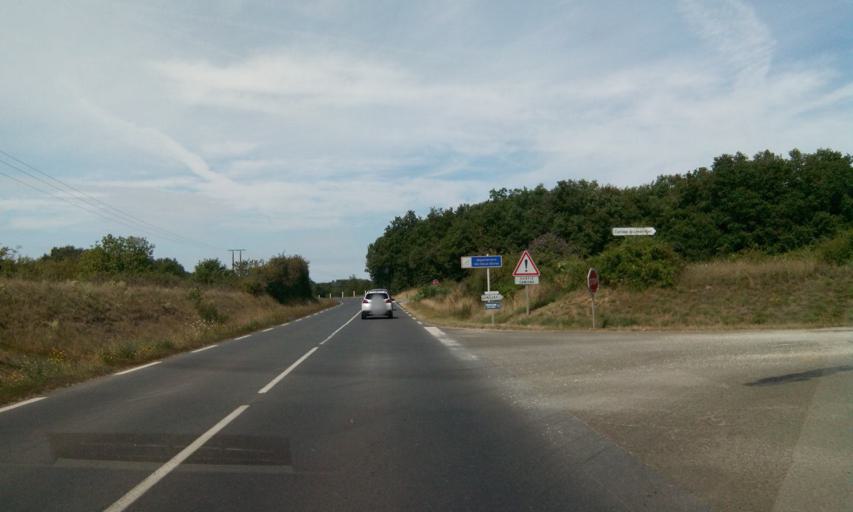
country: FR
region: Poitou-Charentes
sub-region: Departement de la Vienne
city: Civray
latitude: 46.1423
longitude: 0.2162
